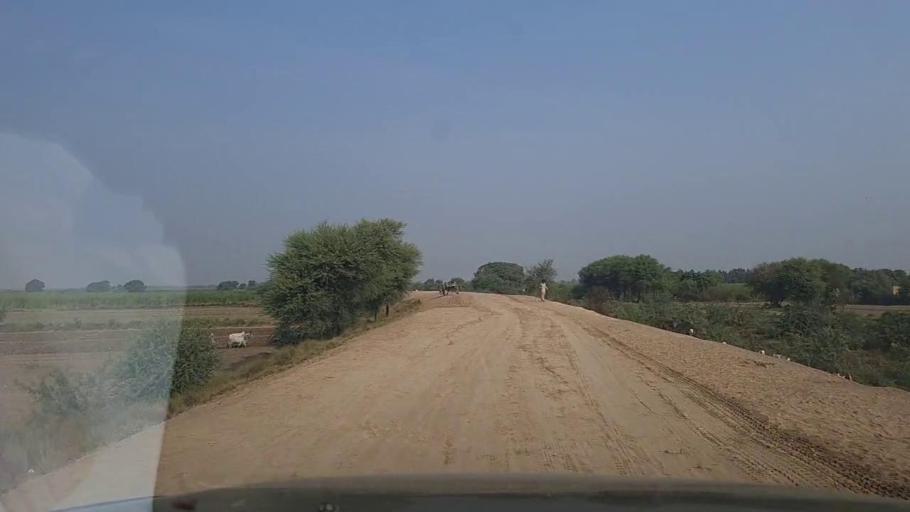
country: PK
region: Sindh
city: Bulri
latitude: 24.9863
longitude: 68.2939
